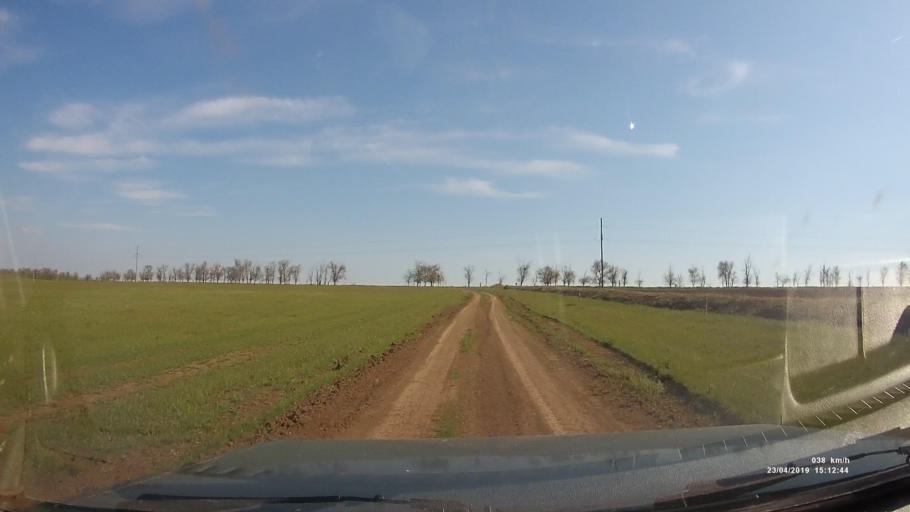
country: RU
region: Rostov
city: Remontnoye
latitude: 46.5423
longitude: 42.9507
